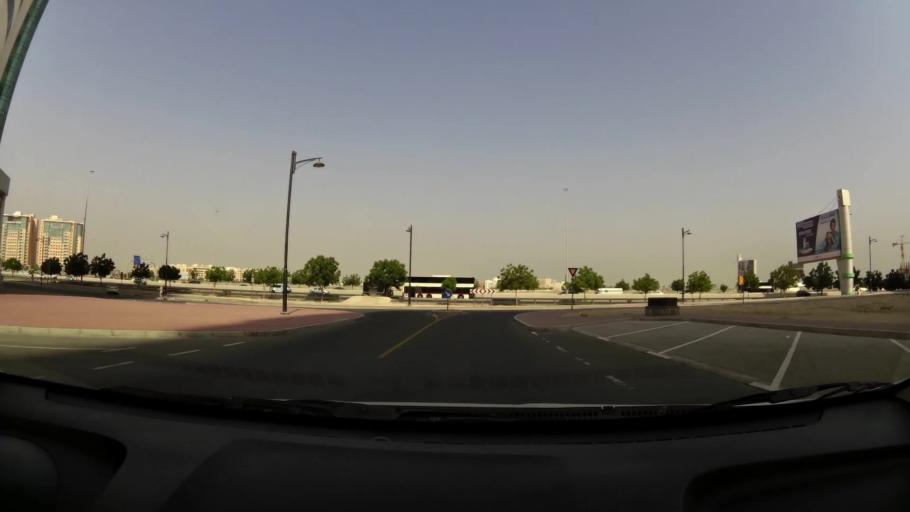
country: AE
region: Ash Shariqah
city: Sharjah
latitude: 25.2934
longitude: 55.3615
